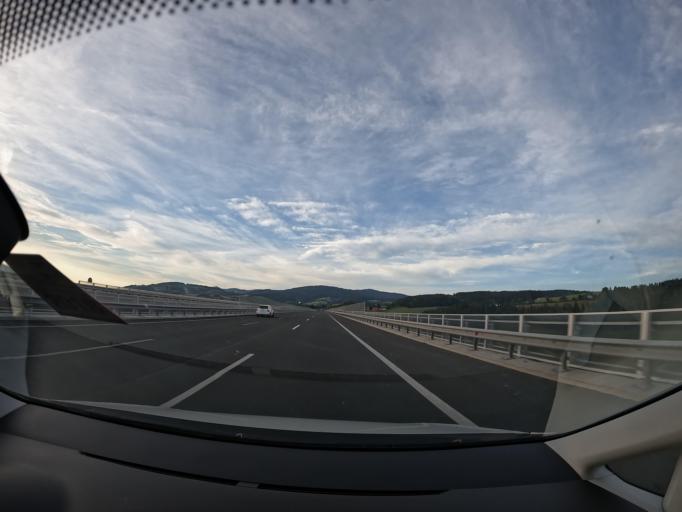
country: AT
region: Carinthia
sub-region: Politischer Bezirk Wolfsberg
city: Bad Sankt Leonhard im Lavanttal
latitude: 46.9261
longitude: 14.8228
